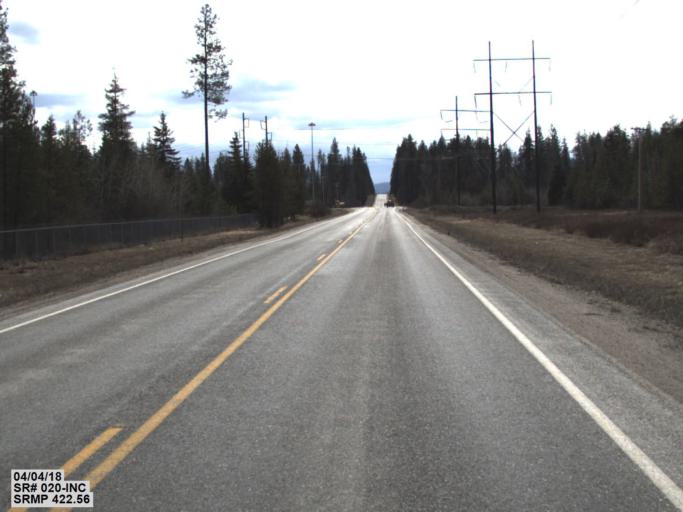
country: US
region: Washington
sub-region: Pend Oreille County
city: Newport
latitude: 48.2909
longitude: -117.2743
